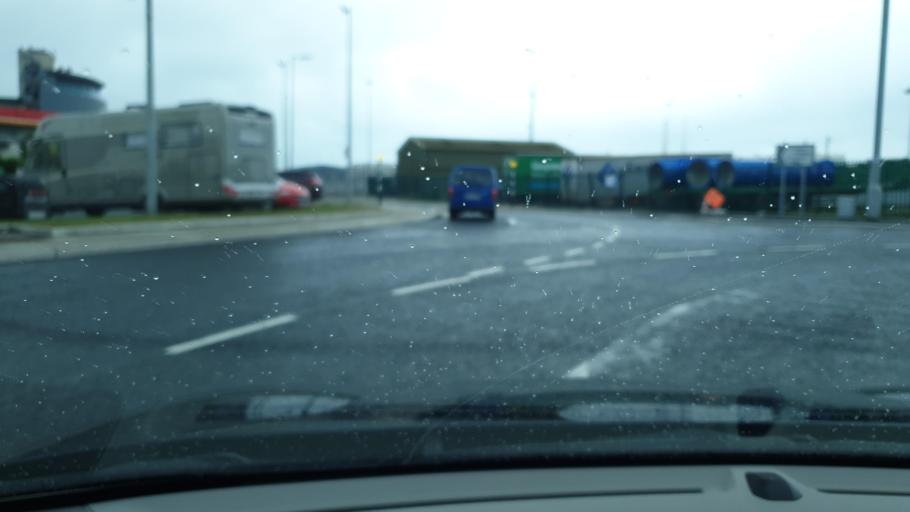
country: IE
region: Leinster
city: Ringsend
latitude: 53.3538
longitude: -6.2138
